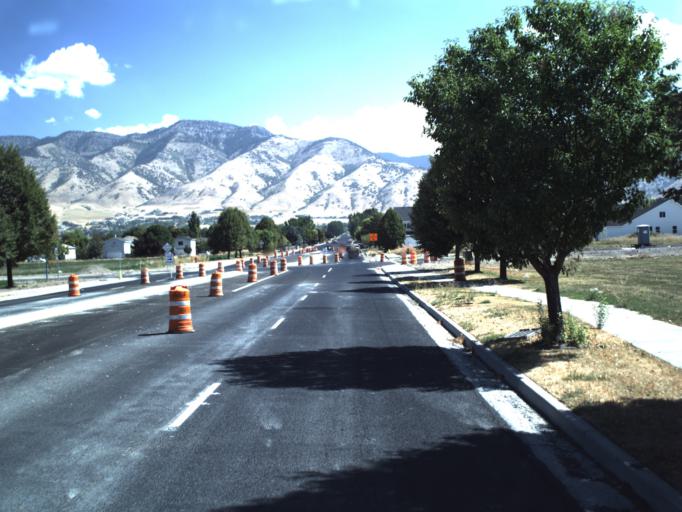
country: US
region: Utah
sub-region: Cache County
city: Hyde Park
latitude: 41.7777
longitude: -111.8317
